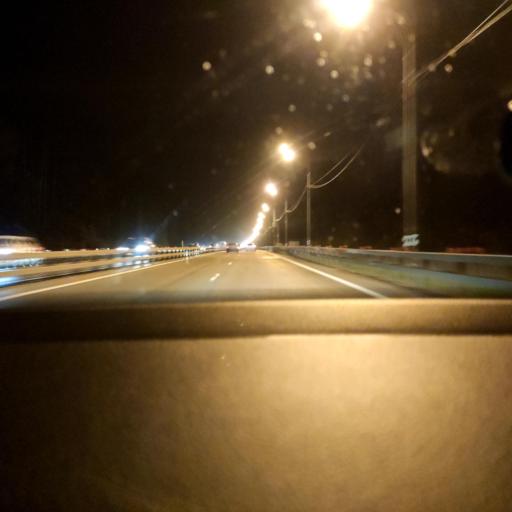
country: RU
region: Moskovskaya
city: Selyatino
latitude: 55.4992
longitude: 36.9699
